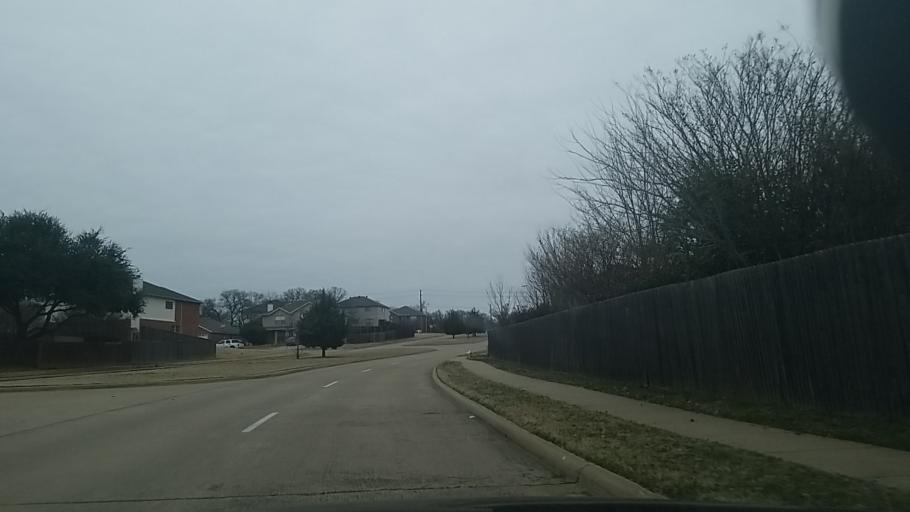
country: US
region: Texas
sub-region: Denton County
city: Corinth
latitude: 33.1400
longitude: -97.0784
